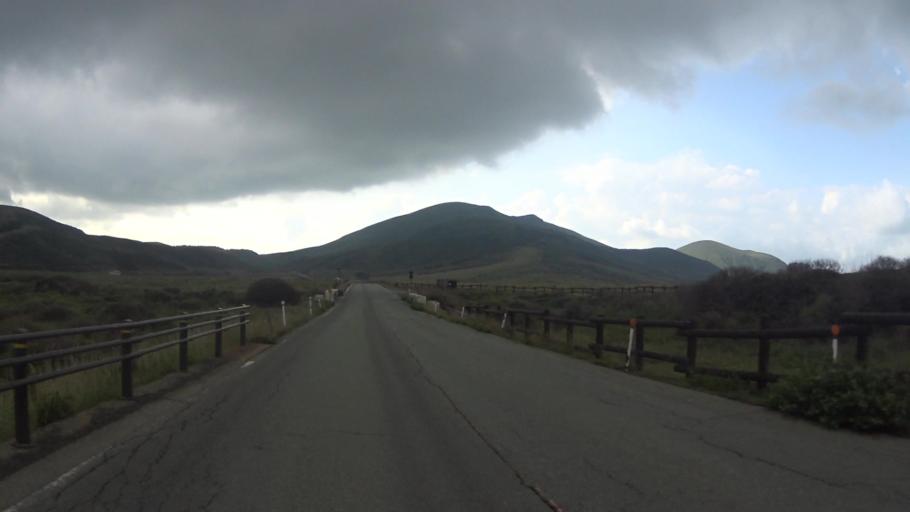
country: JP
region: Kumamoto
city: Aso
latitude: 32.8810
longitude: 131.0708
